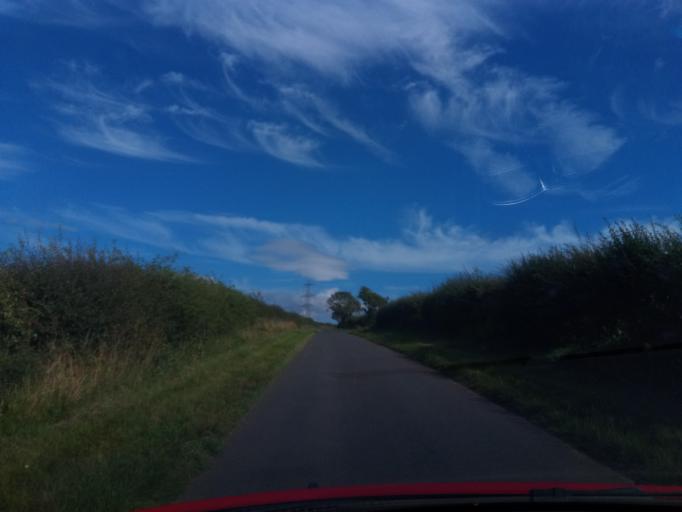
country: GB
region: Scotland
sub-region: The Scottish Borders
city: Coldstream
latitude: 55.6185
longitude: -2.1857
